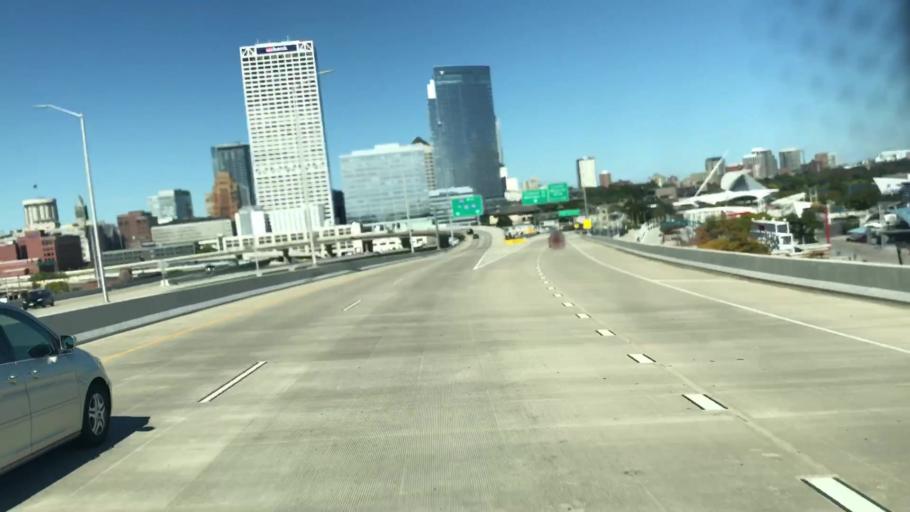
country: US
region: Wisconsin
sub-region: Milwaukee County
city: Milwaukee
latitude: 43.0313
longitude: -87.9002
